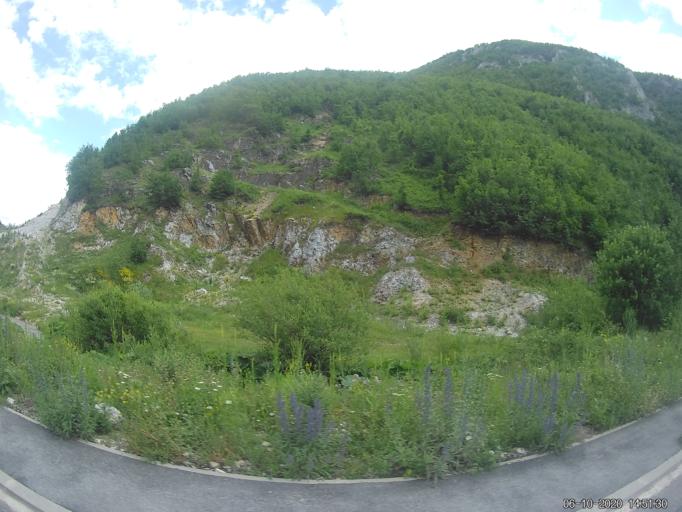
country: XK
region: Prizren
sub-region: Komuna e Therandes
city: Budakovo
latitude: 42.3996
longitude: 20.9752
